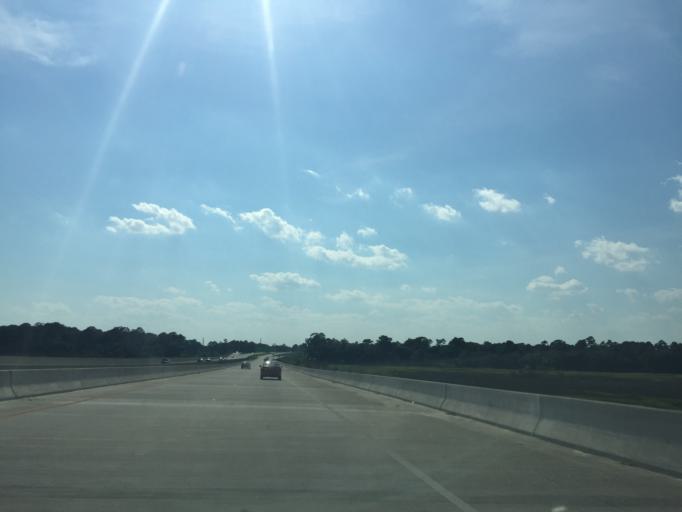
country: US
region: Georgia
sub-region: Chatham County
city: Montgomery
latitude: 31.9755
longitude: -81.1212
